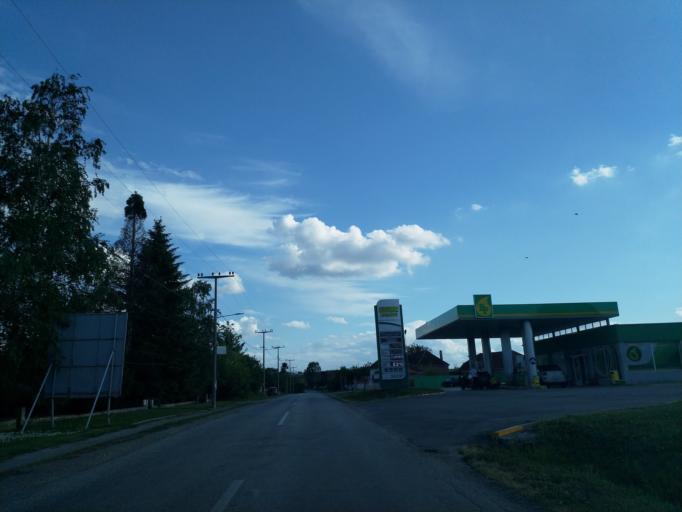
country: RS
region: Central Serbia
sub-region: Sumadijski Okrug
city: Lapovo
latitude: 44.1773
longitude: 21.0909
